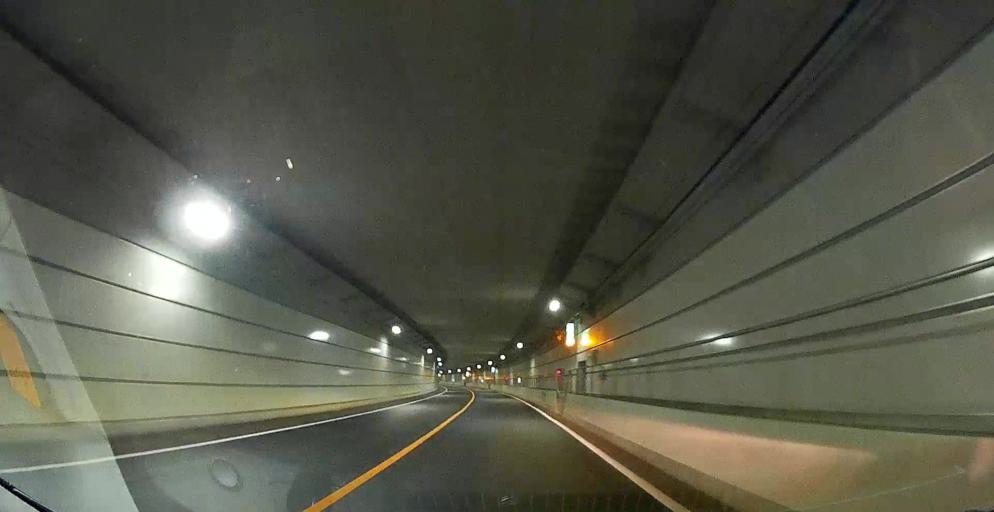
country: JP
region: Tokyo
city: Urayasu
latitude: 35.6135
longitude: 139.7973
